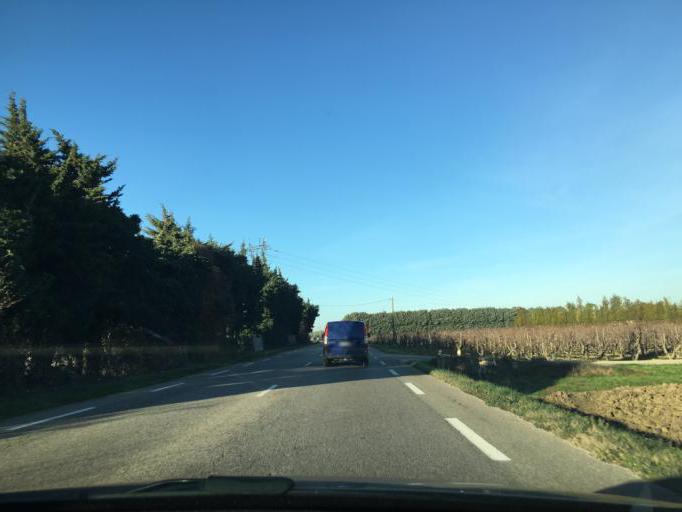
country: FR
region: Provence-Alpes-Cote d'Azur
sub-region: Departement du Vaucluse
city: Le Thor
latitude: 43.8841
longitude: 4.9929
